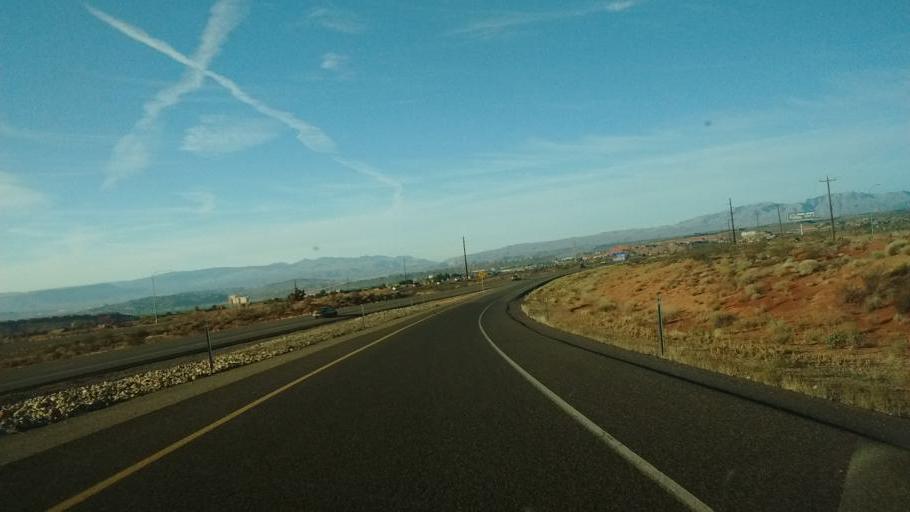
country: US
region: Utah
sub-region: Washington County
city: Washington
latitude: 37.1468
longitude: -113.4902
